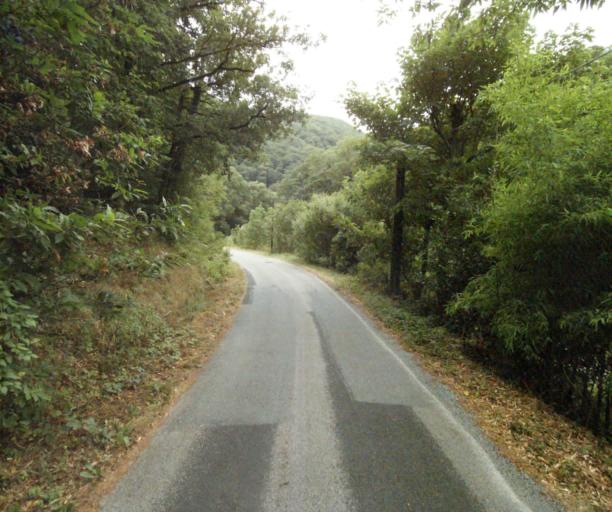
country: FR
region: Midi-Pyrenees
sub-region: Departement du Tarn
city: Soreze
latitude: 43.4282
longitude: 2.0801
